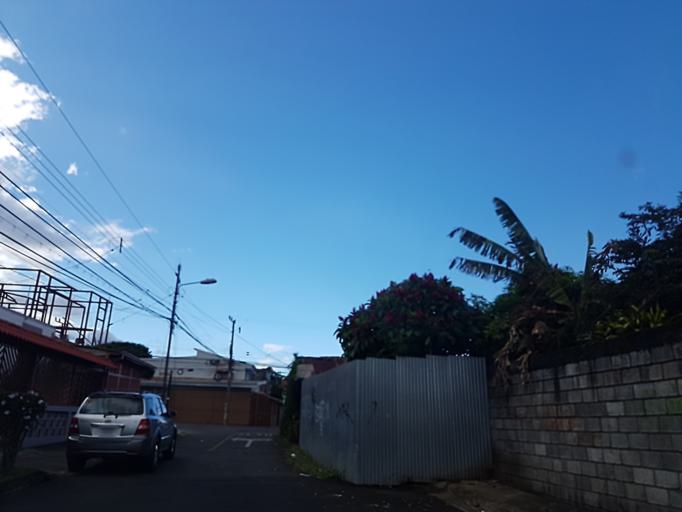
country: CR
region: San Jose
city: San Pedro
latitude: 9.9234
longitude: -84.0536
